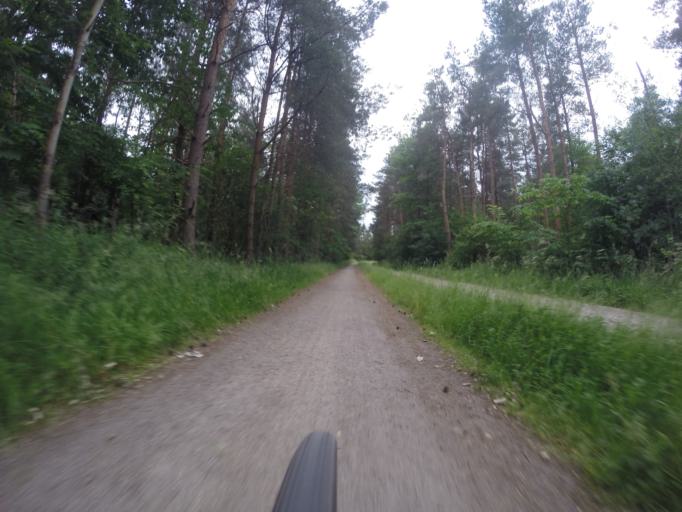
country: DK
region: Capital Region
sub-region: Ballerup Kommune
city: Ballerup
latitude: 55.7033
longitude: 12.3477
